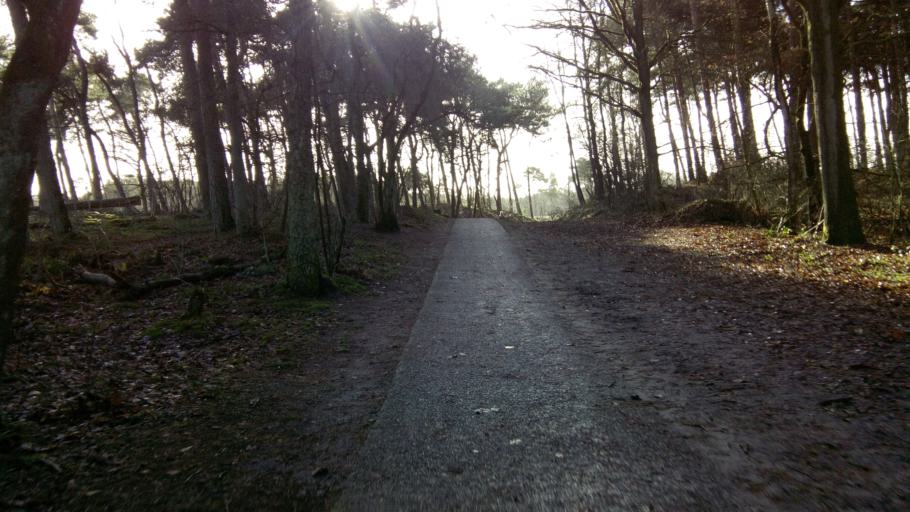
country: NL
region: Gelderland
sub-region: Gemeente Nijmegen
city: Lindenholt
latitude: 51.7878
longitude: 5.7970
